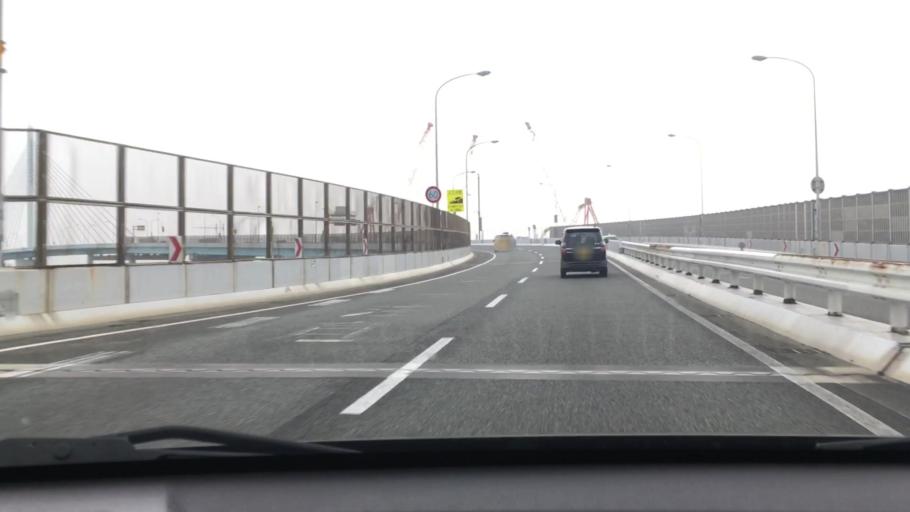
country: JP
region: Fukuoka
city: Fukuoka-shi
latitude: 33.5998
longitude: 130.3779
